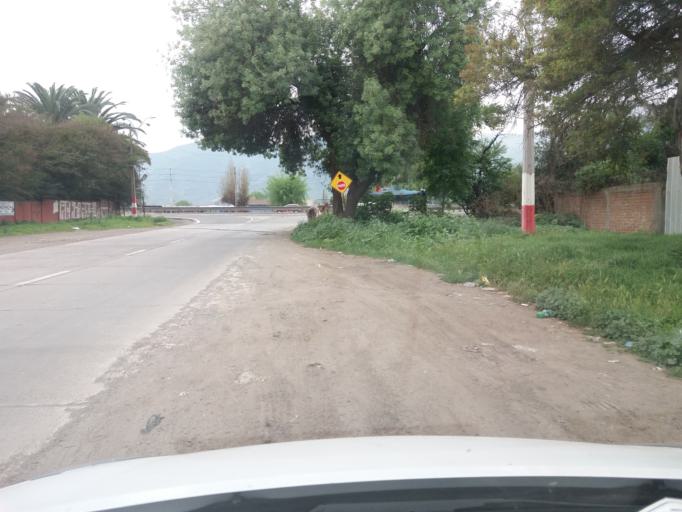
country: CL
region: Valparaiso
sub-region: Provincia de Quillota
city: Hacienda La Calera
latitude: -32.7781
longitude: -71.1817
